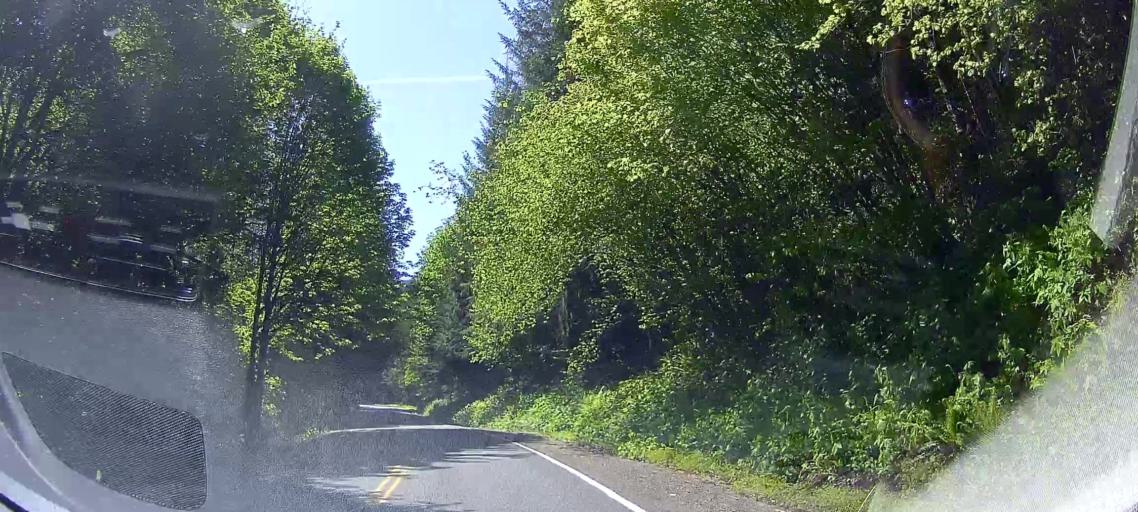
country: US
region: Washington
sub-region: Snohomish County
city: Darrington
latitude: 48.4625
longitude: -121.6142
